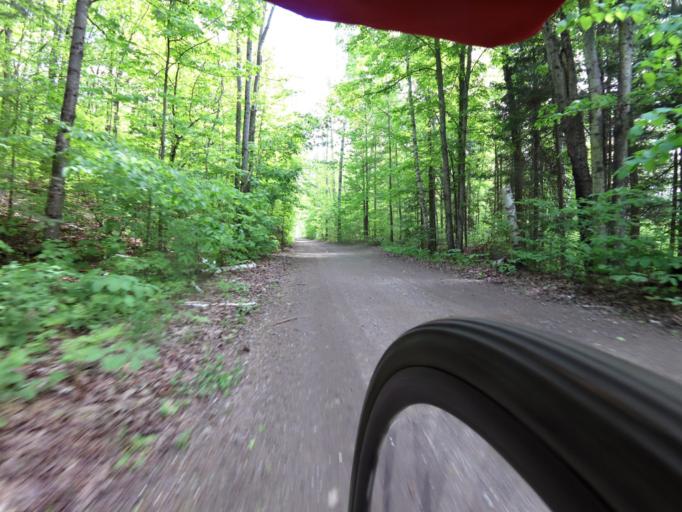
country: CA
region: Ontario
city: Renfrew
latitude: 45.1992
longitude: -76.6852
